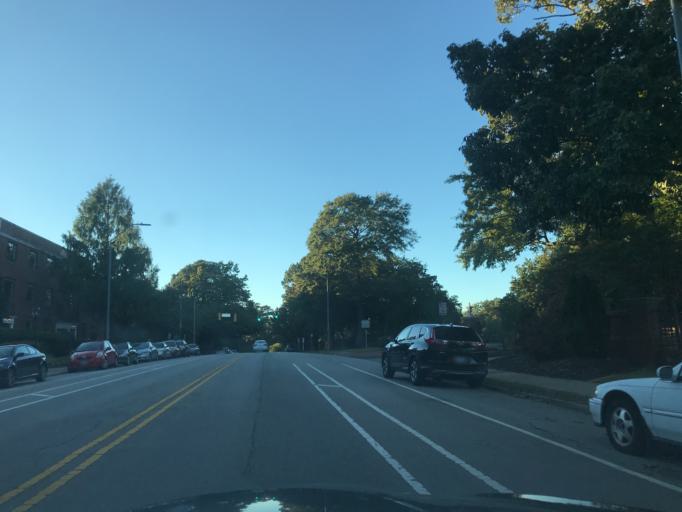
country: US
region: North Carolina
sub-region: Wake County
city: West Raleigh
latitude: 35.7813
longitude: -78.6525
